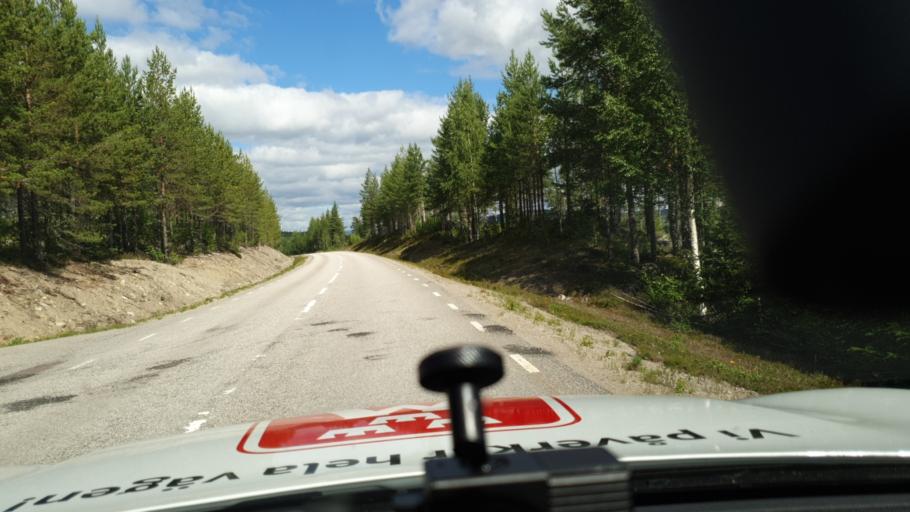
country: NO
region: Hedmark
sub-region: Trysil
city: Innbygda
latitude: 61.0191
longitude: 12.5371
